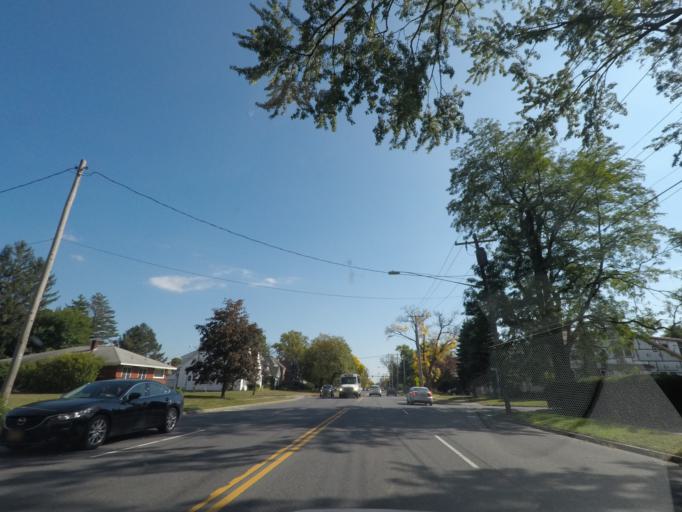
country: US
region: New York
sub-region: Albany County
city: West Albany
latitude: 42.6761
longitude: -73.7967
